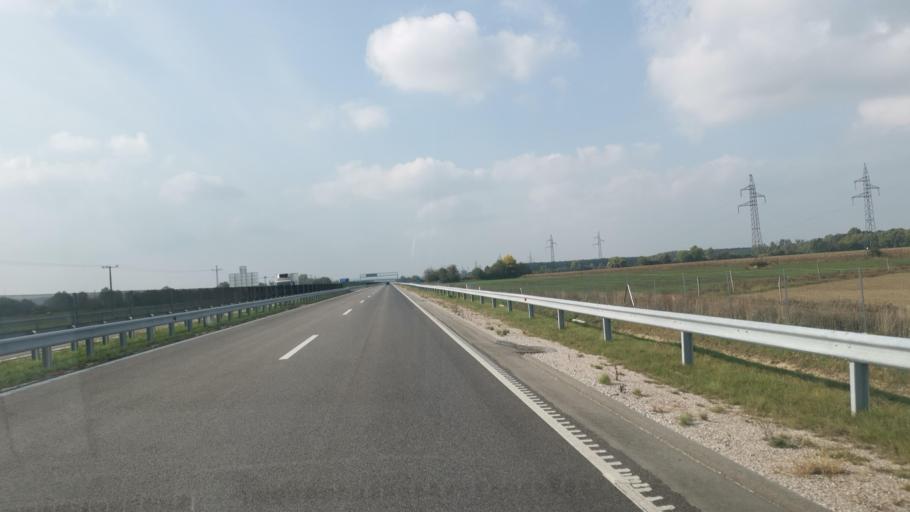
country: HU
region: Gyor-Moson-Sopron
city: Fertoszentmiklos
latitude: 47.5693
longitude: 16.8449
